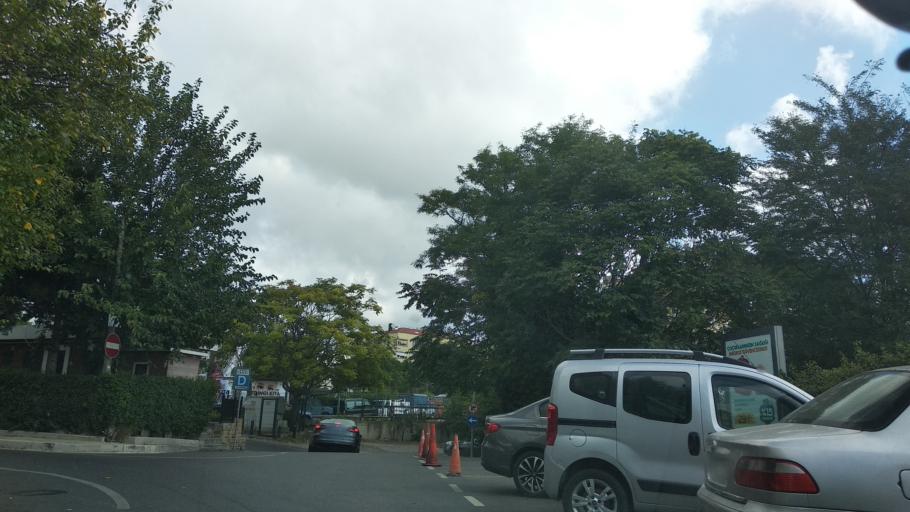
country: TR
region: Istanbul
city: Sisli
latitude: 41.0844
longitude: 29.0410
